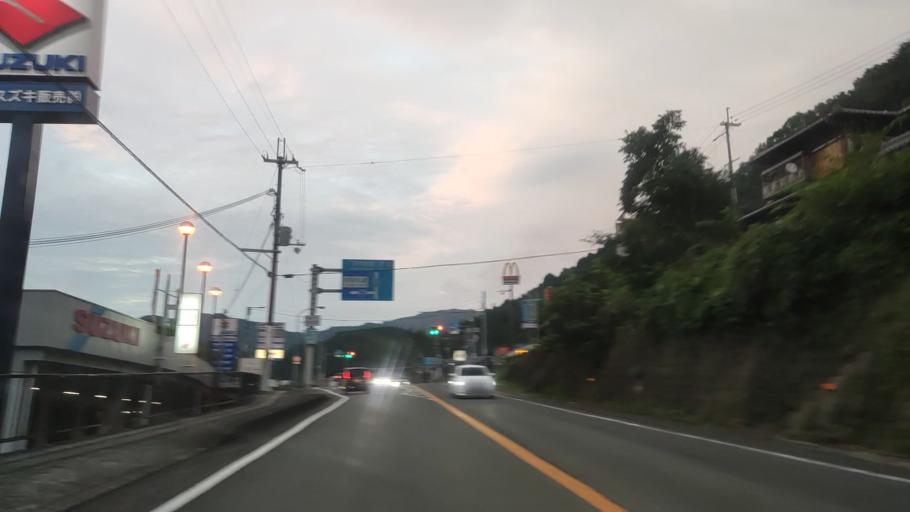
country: JP
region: Wakayama
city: Hashimoto
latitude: 34.3572
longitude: 135.6069
